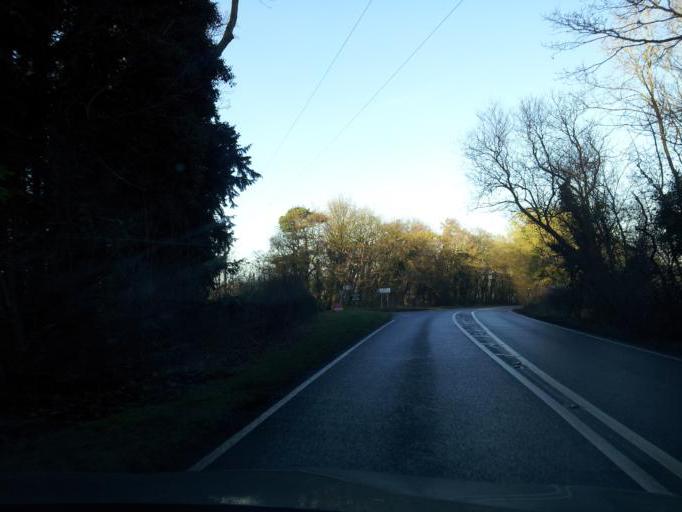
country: GB
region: England
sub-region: Suffolk
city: Lavenham
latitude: 52.1440
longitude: 0.7585
